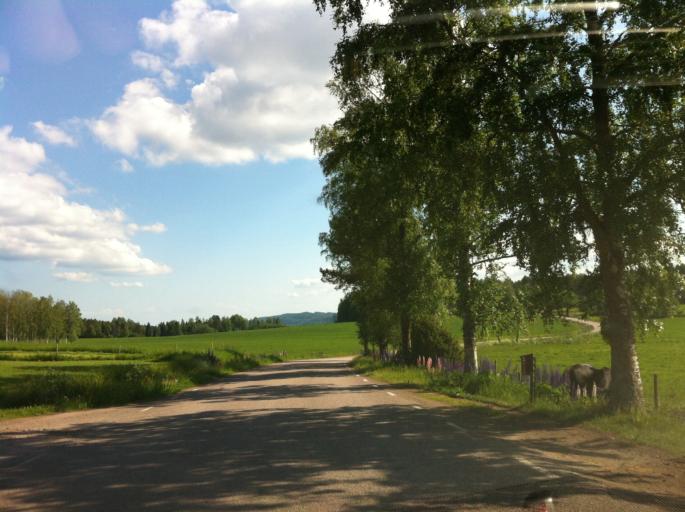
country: SE
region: Vaermland
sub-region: Sunne Kommun
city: Sunne
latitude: 59.7197
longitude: 13.2254
